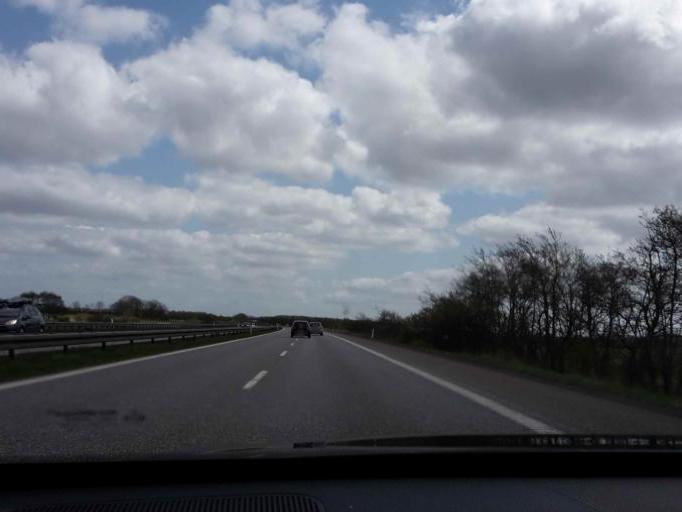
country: DK
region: South Denmark
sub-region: Esbjerg Kommune
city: Bramming
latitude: 55.5087
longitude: 8.6505
